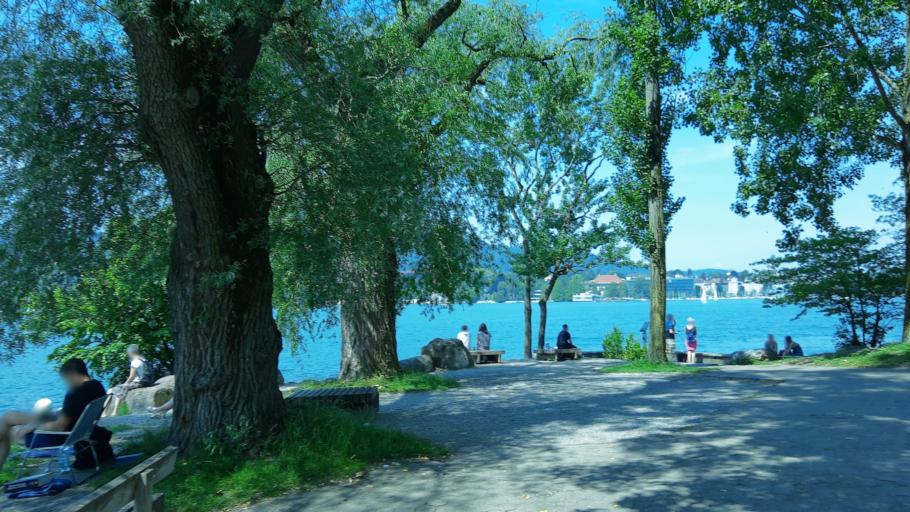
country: CH
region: Zurich
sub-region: Bezirk Zuerich
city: Zuerich (Kreis 8) / Seefeld
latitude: 47.3579
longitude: 8.5477
